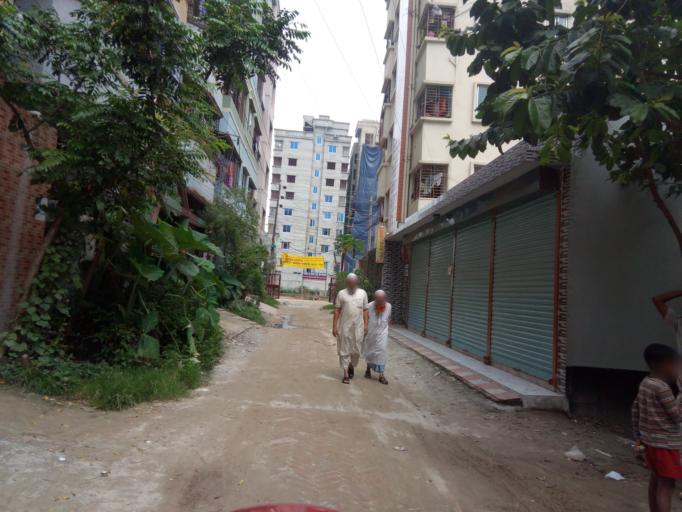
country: BD
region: Dhaka
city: Paltan
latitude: 23.7574
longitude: 90.4434
